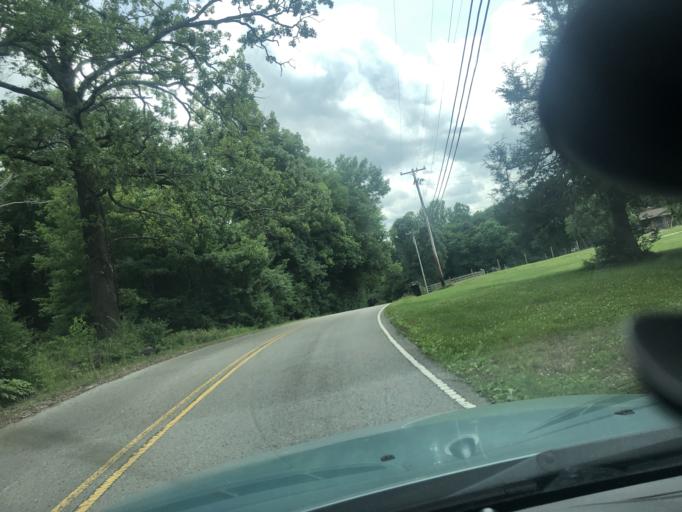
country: US
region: Tennessee
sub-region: Rutherford County
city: La Vergne
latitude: 36.1204
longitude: -86.6337
